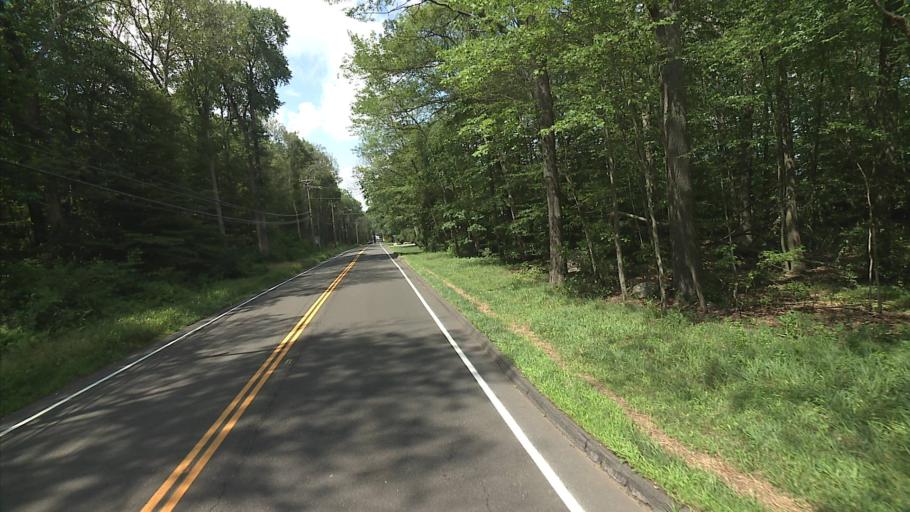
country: US
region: Connecticut
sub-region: New Haven County
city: Madison
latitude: 41.3770
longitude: -72.5657
